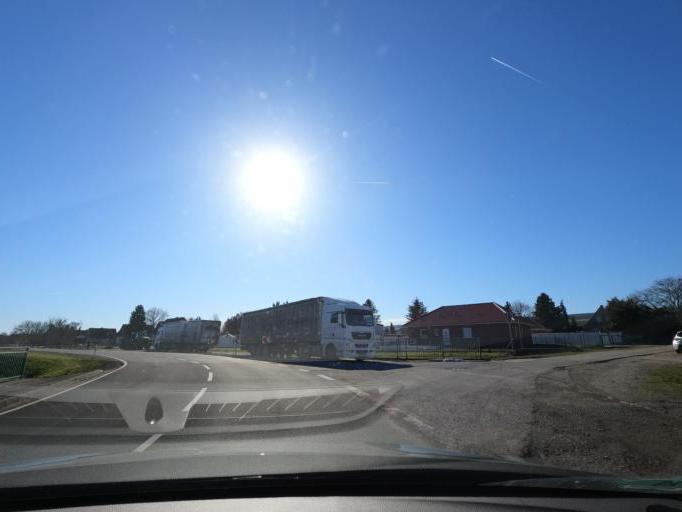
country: DE
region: Lower Saxony
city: Winnigstedt
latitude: 52.0222
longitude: 10.7743
